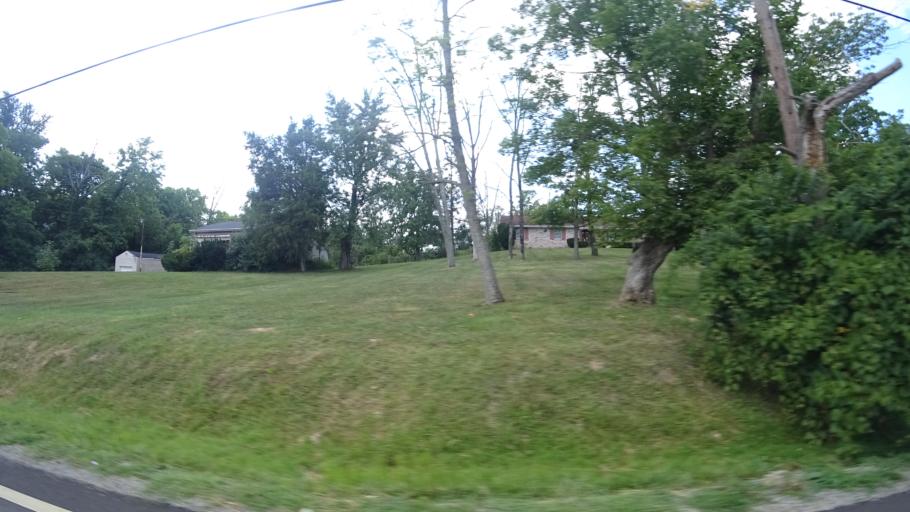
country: US
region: Ohio
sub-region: Butler County
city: Hamilton
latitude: 39.4326
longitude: -84.6026
